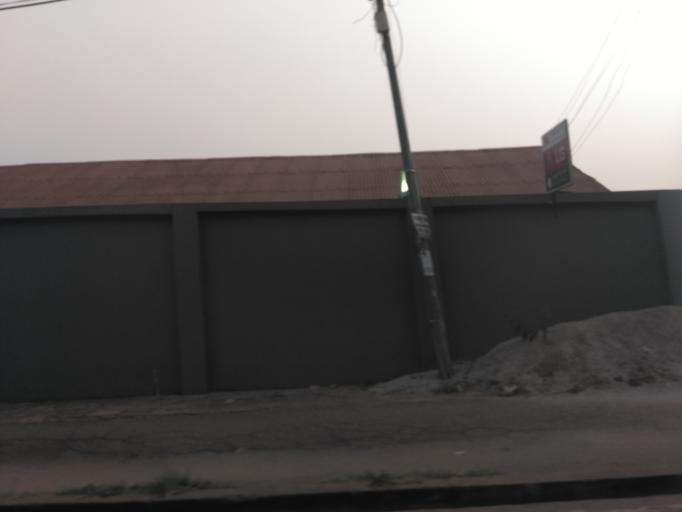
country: GH
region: Ashanti
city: Kumasi
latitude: 6.6845
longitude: -1.6170
